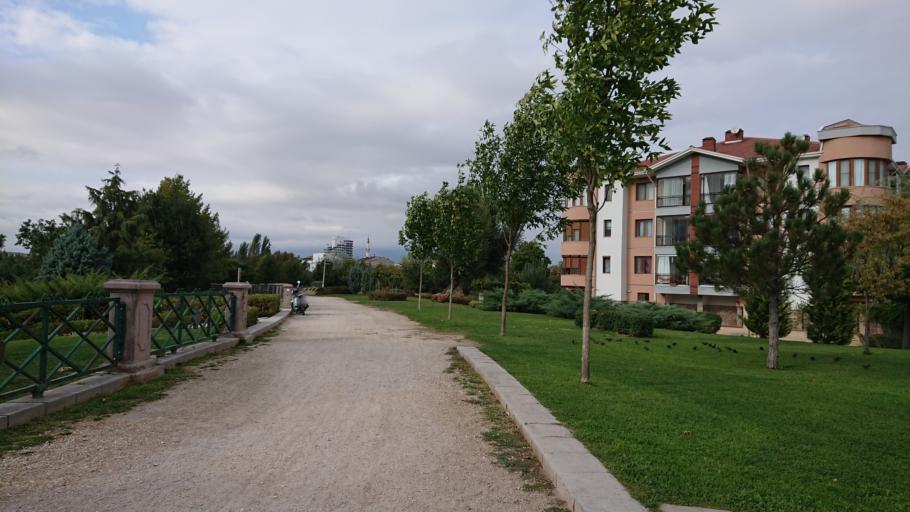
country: TR
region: Eskisehir
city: Eskisehir
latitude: 39.7631
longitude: 30.4866
